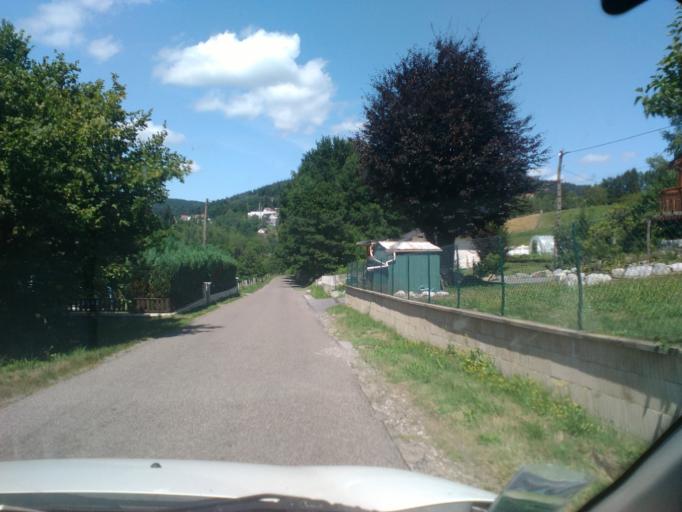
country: FR
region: Lorraine
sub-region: Departement des Vosges
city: Le Tholy
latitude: 48.0747
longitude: 6.7441
